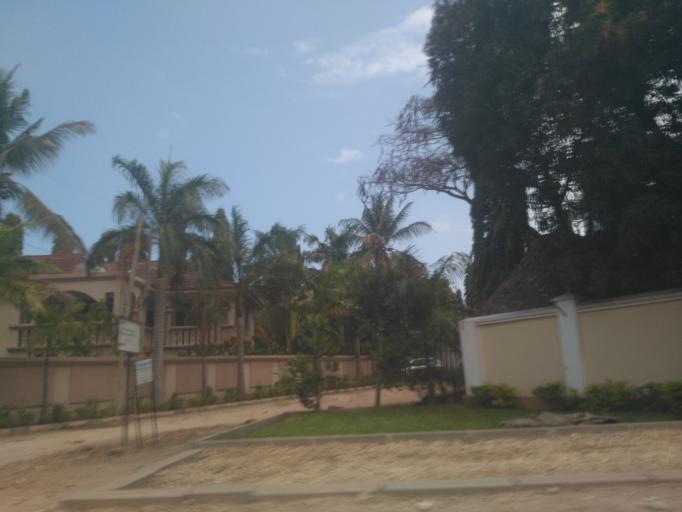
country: TZ
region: Dar es Salaam
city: Magomeni
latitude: -6.7505
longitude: 39.2810
